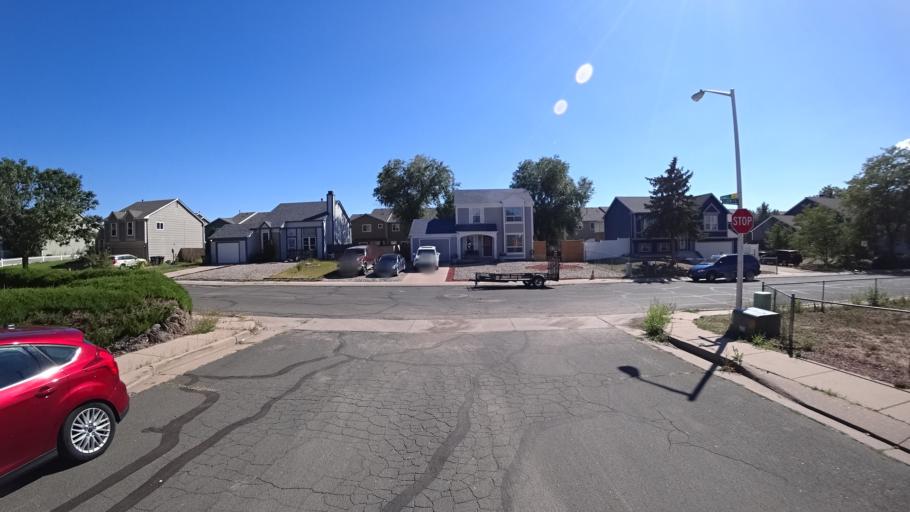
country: US
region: Colorado
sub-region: El Paso County
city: Stratmoor
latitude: 38.7909
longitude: -104.7375
